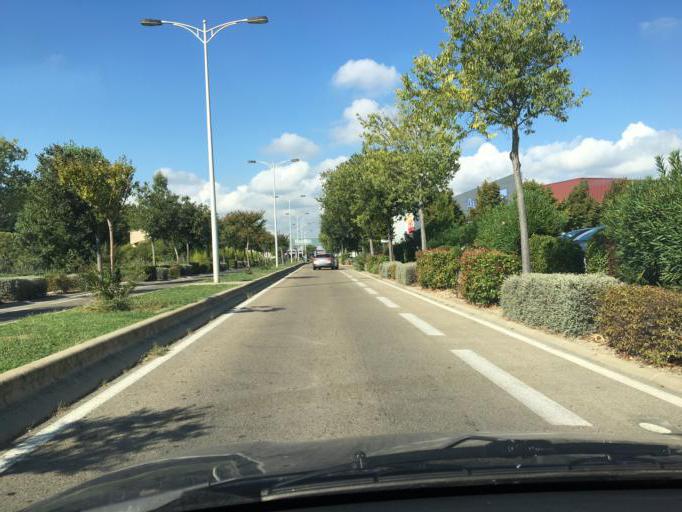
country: FR
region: Languedoc-Roussillon
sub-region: Departement du Gard
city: Caissargues
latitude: 43.8078
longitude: 4.3648
